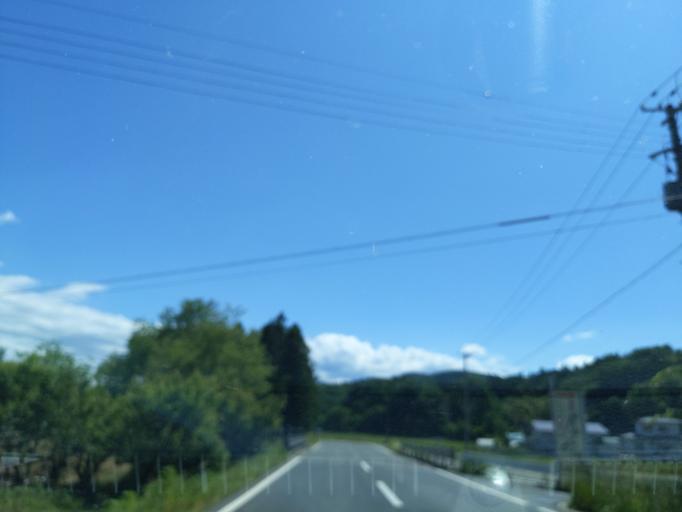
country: JP
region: Fukushima
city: Koriyama
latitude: 37.3876
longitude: 140.2618
